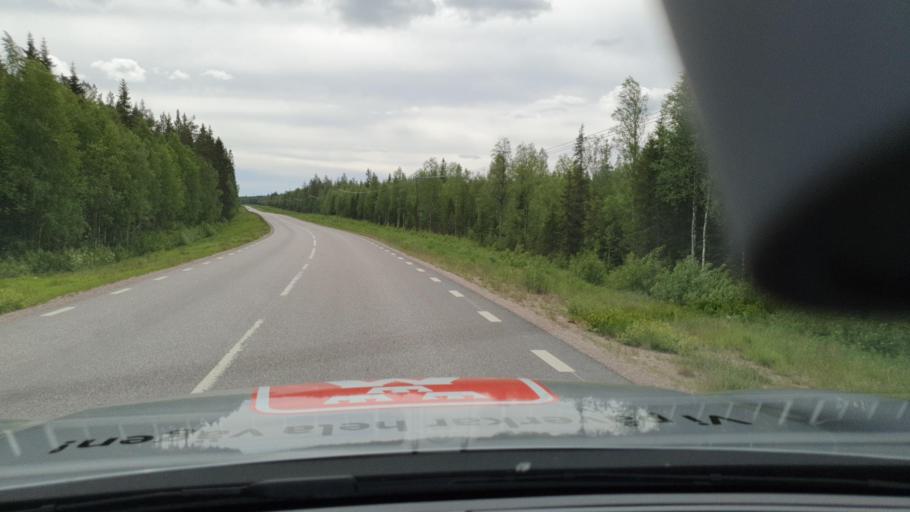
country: SE
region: Norrbotten
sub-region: Kalix Kommun
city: Kalix
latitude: 65.9108
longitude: 23.4549
